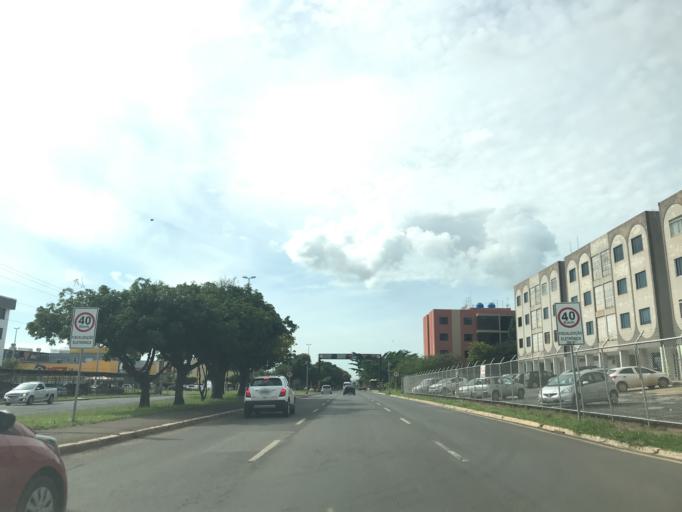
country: BR
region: Federal District
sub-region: Brasilia
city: Brasilia
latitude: -15.8119
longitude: -48.0896
